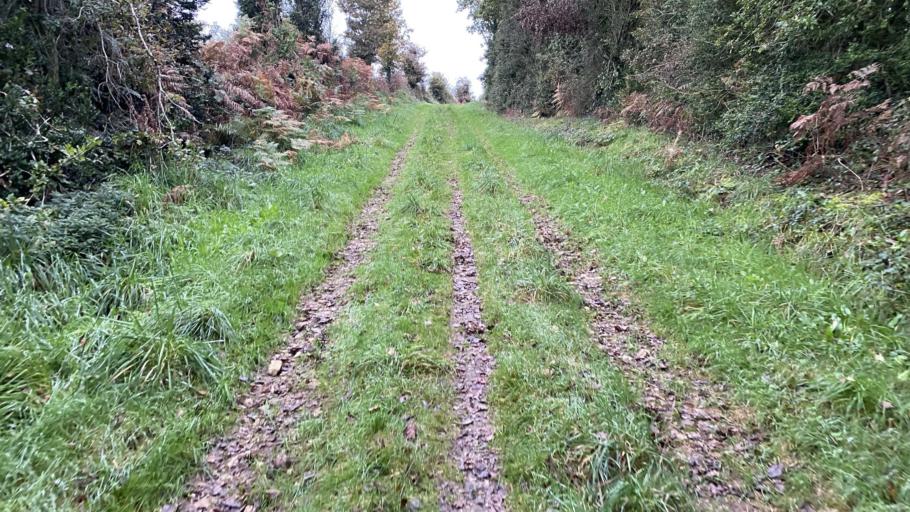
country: FR
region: Brittany
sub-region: Departement du Finistere
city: Daoulas
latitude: 48.3527
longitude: -4.2513
